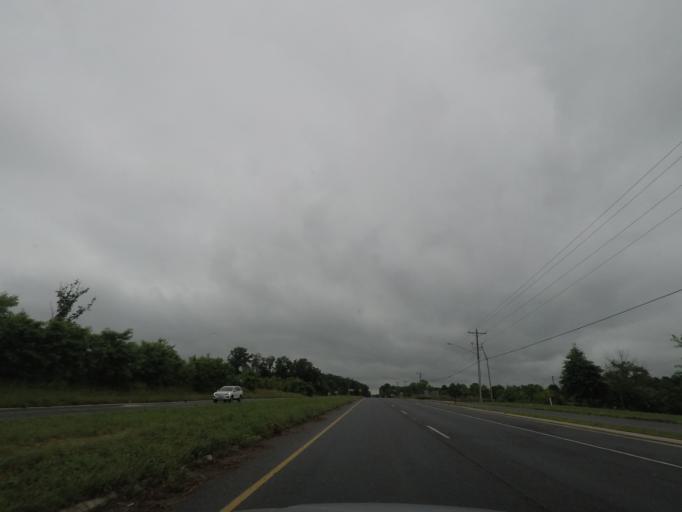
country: US
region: Virginia
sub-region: Prince William County
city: Bull Run Mountain Estates
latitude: 38.8711
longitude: -77.6354
